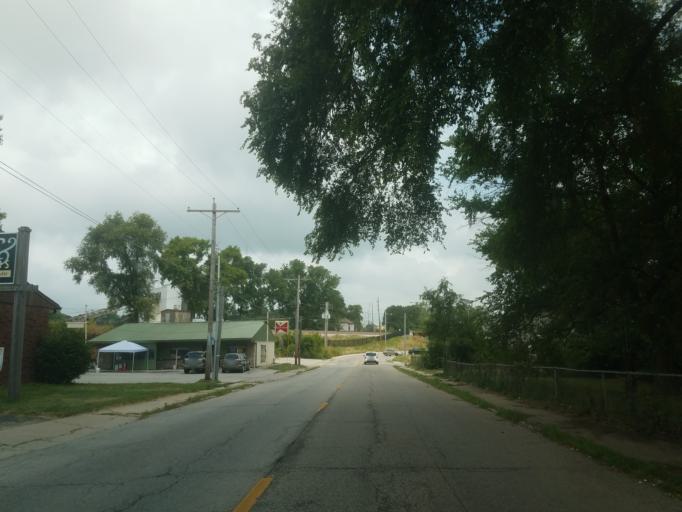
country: US
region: Illinois
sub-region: McLean County
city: Bloomington
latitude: 40.4804
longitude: -89.0066
